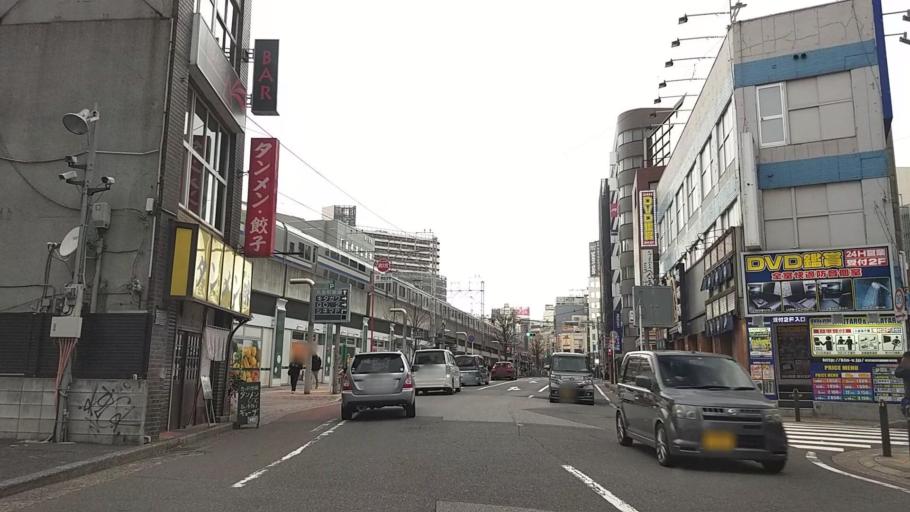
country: JP
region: Chiba
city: Chiba
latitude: 35.6085
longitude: 140.1178
